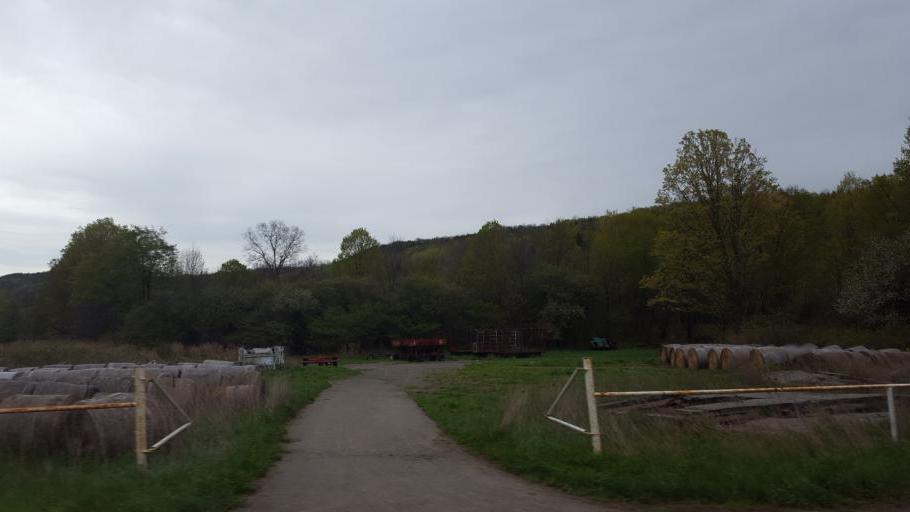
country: US
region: Pennsylvania
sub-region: Tioga County
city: Westfield
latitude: 42.0478
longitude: -77.4664
